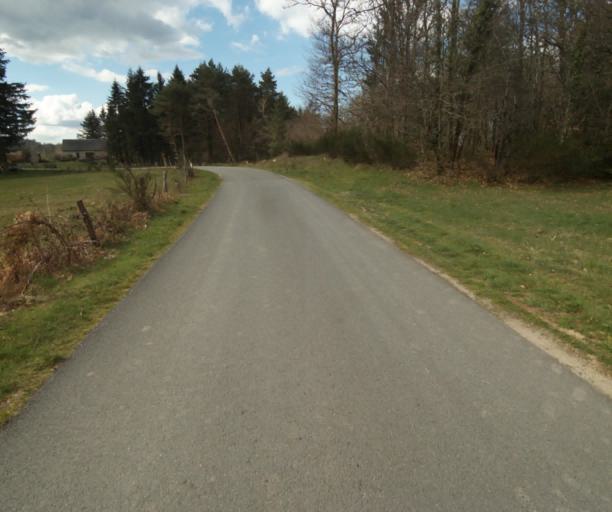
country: FR
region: Limousin
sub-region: Departement de la Correze
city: Correze
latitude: 45.2765
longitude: 1.8976
